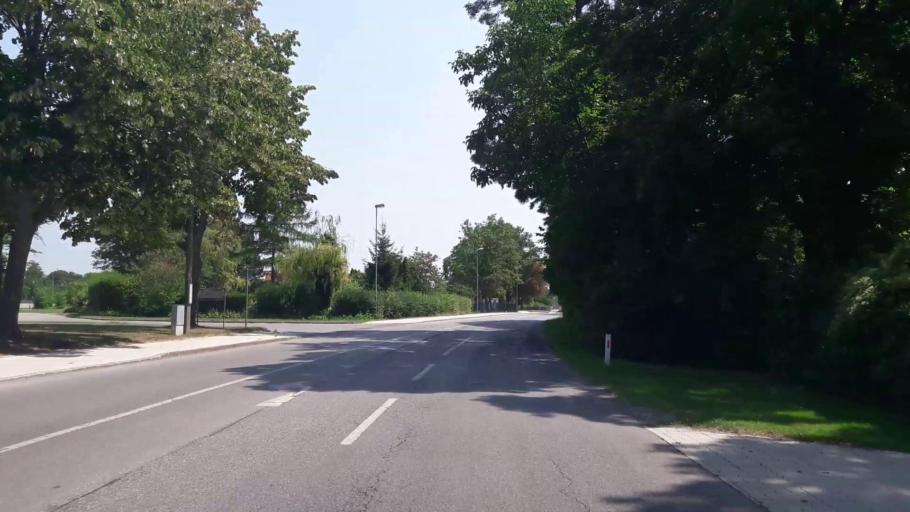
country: AT
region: Lower Austria
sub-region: Politischer Bezirk Bruck an der Leitha
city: Trautmannsdorf an der Leitha
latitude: 48.0238
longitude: 16.6418
